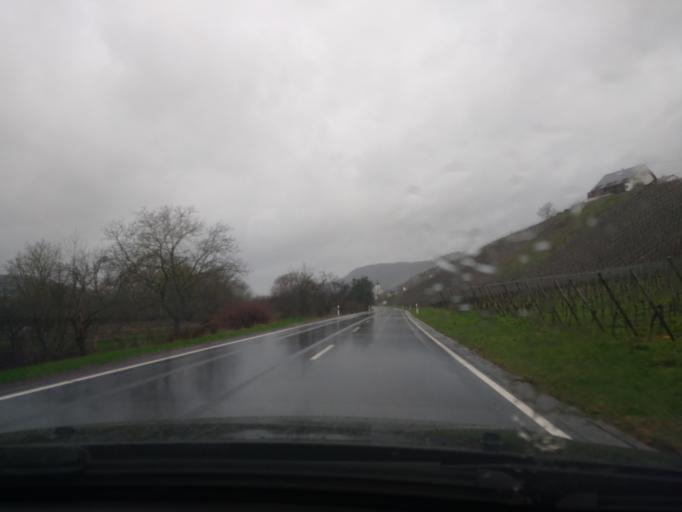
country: DE
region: Rheinland-Pfalz
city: Kinheim
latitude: 49.9703
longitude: 7.0648
